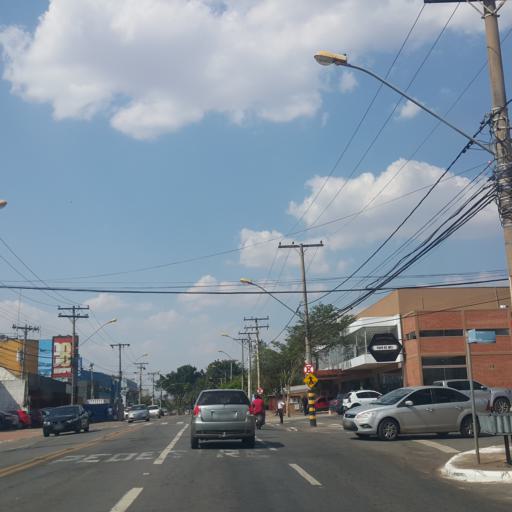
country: BR
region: Goias
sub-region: Goiania
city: Goiania
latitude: -16.6905
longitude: -49.2560
